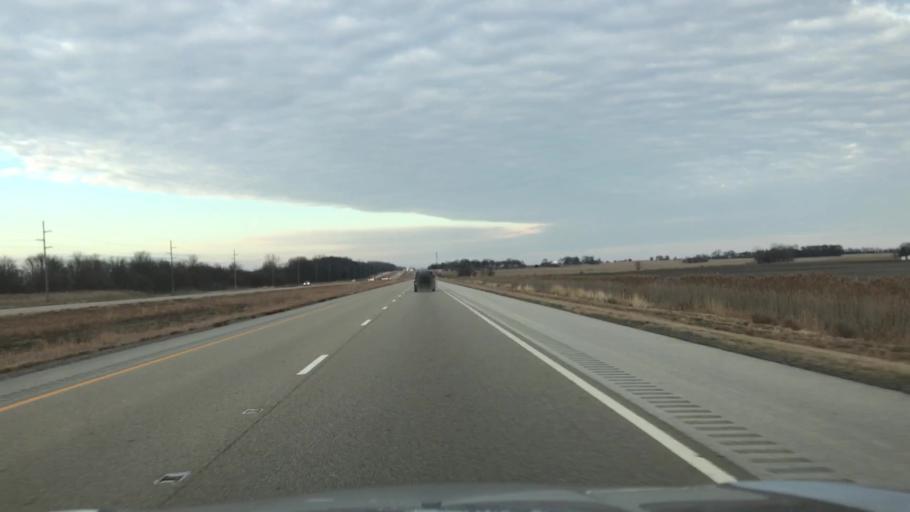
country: US
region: Illinois
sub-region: Logan County
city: Atlanta
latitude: 40.2262
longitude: -89.2712
